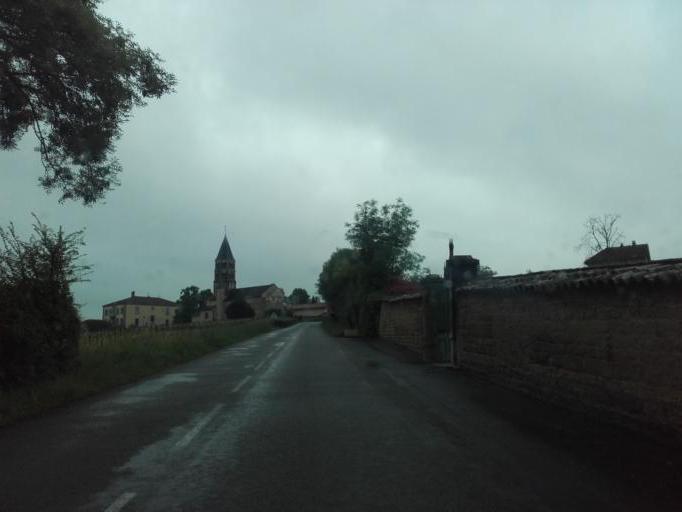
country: FR
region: Bourgogne
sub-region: Departement de Saone-et-Loire
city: Creches-sur-Saone
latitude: 46.2539
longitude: 4.7554
